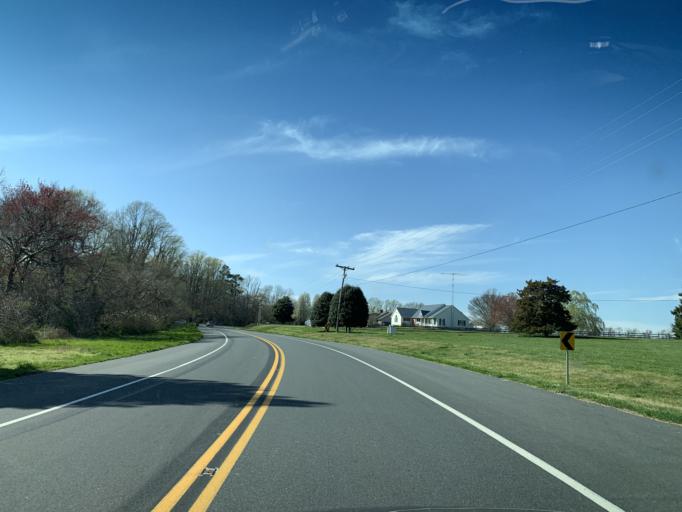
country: US
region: Delaware
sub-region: Kent County
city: Riverview
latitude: 38.9899
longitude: -75.5113
